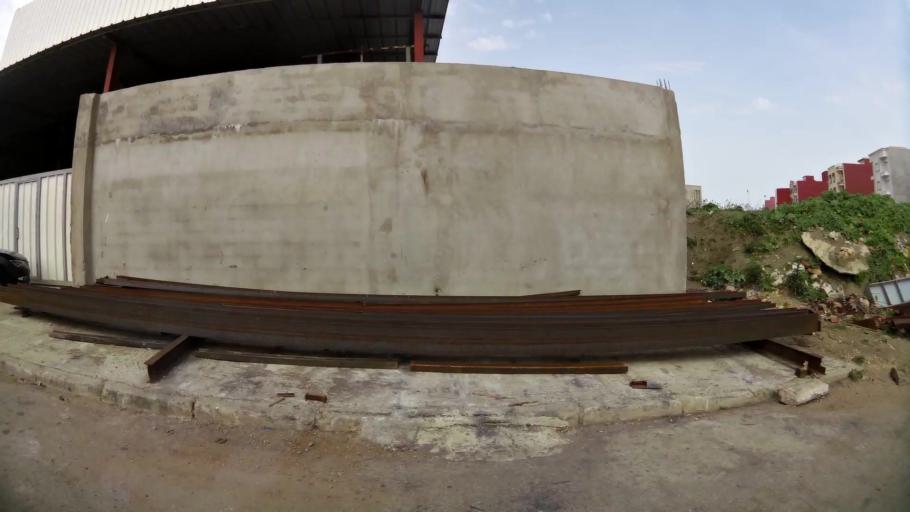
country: MA
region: Tanger-Tetouan
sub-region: Tanger-Assilah
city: Boukhalef
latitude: 35.7115
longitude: -5.8928
